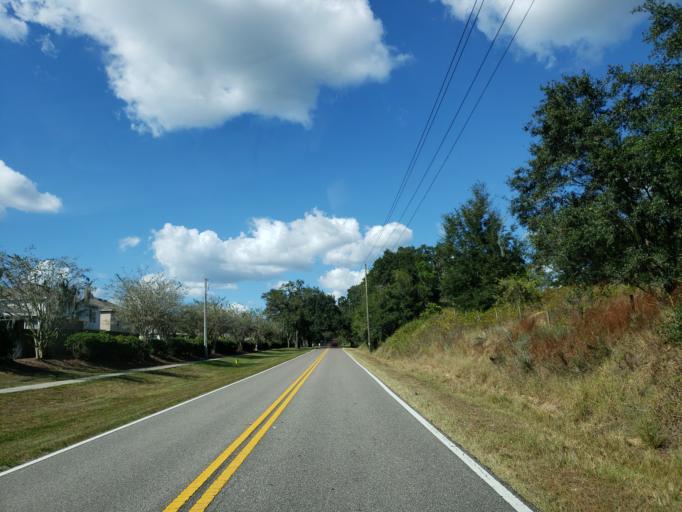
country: US
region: Florida
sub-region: Hillsborough County
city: Valrico
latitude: 27.9188
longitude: -82.2195
